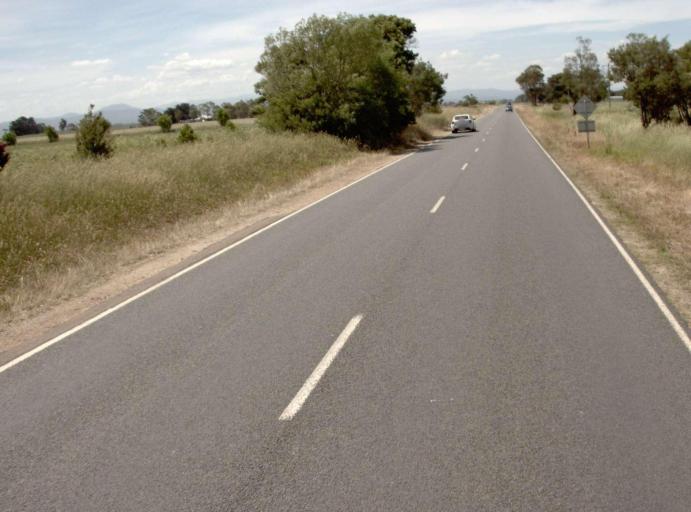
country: AU
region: Victoria
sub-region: Wellington
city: Heyfield
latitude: -38.0034
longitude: 146.8837
